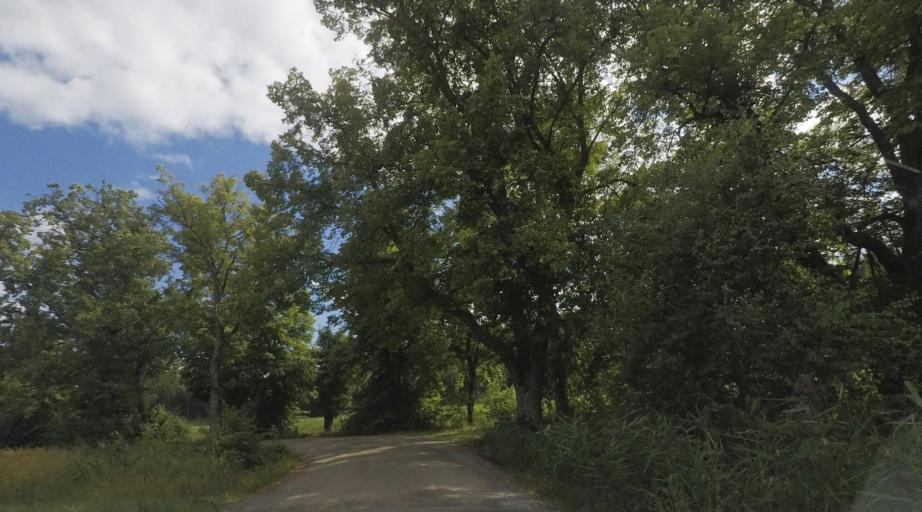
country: SE
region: Stockholm
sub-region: Sodertalje Kommun
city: Pershagen
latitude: 59.1090
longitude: 17.6710
